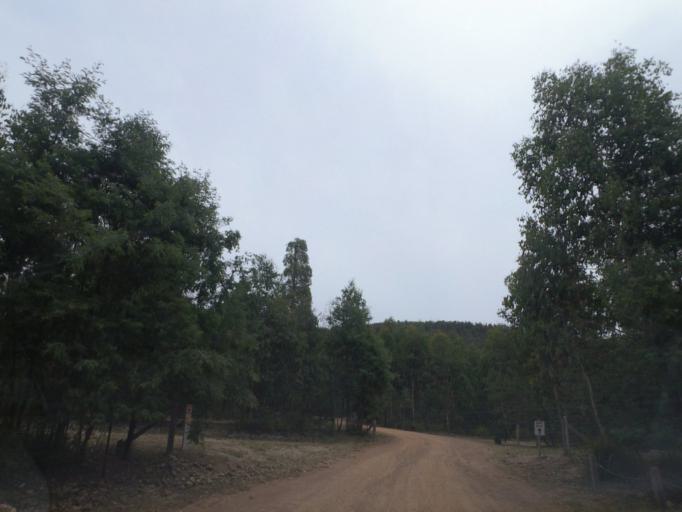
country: AU
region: Victoria
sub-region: Yarra Ranges
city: Healesville
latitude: -37.4267
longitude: 145.5695
